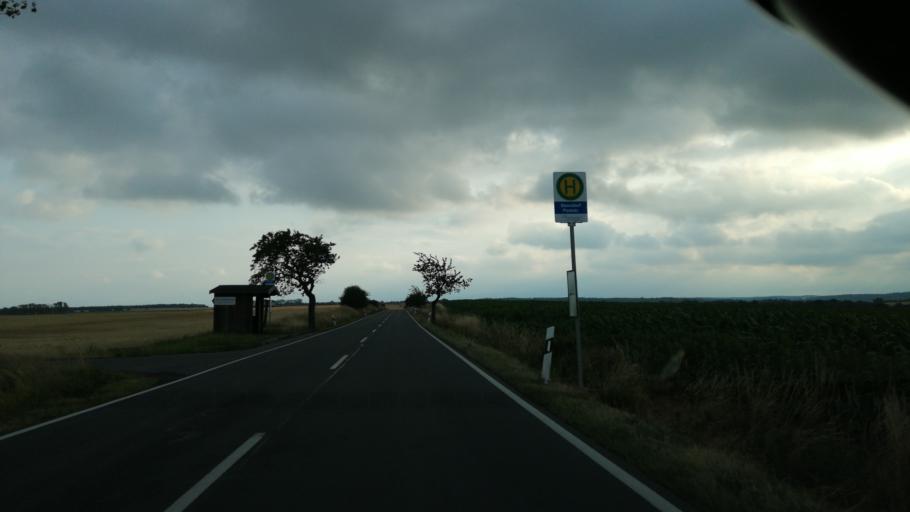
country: DE
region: Saxony-Anhalt
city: Mansfeld
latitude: 51.5759
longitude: 11.4592
